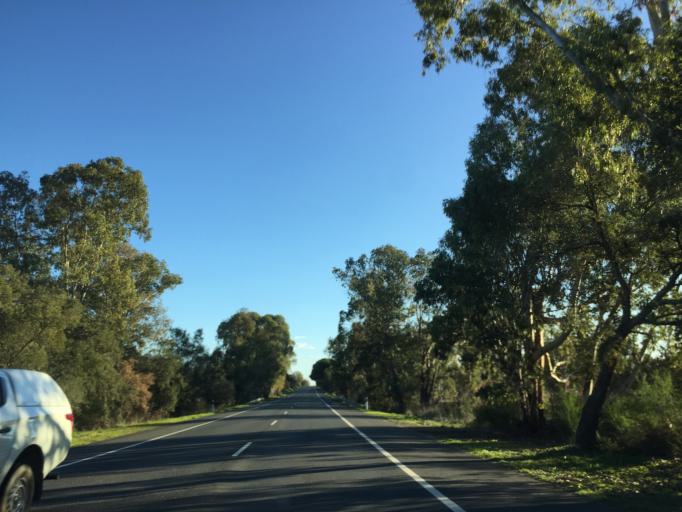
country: PT
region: Setubal
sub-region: Grandola
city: Grandola
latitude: 38.0315
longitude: -8.4002
